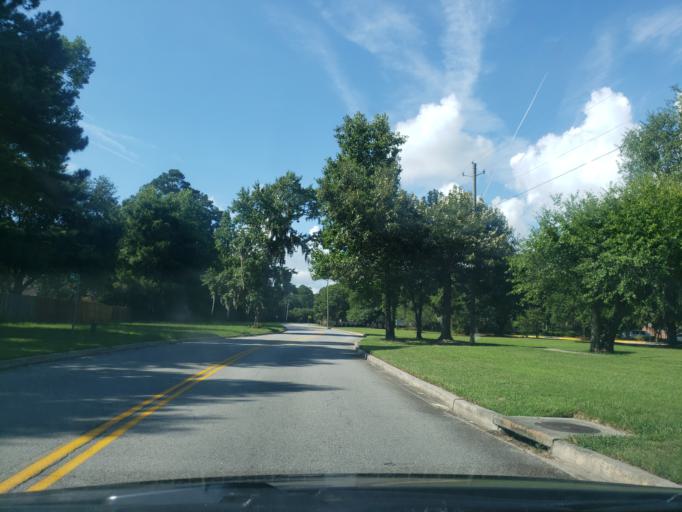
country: US
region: Georgia
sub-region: Chatham County
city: Georgetown
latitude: 31.9767
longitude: -81.2274
